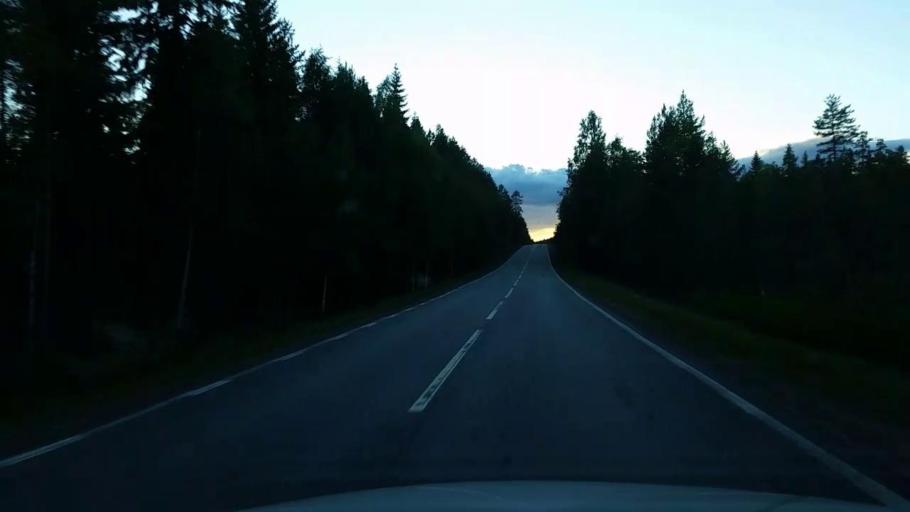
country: SE
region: Gaevleborg
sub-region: Ljusdals Kommun
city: Farila
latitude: 62.0918
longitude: 15.8009
